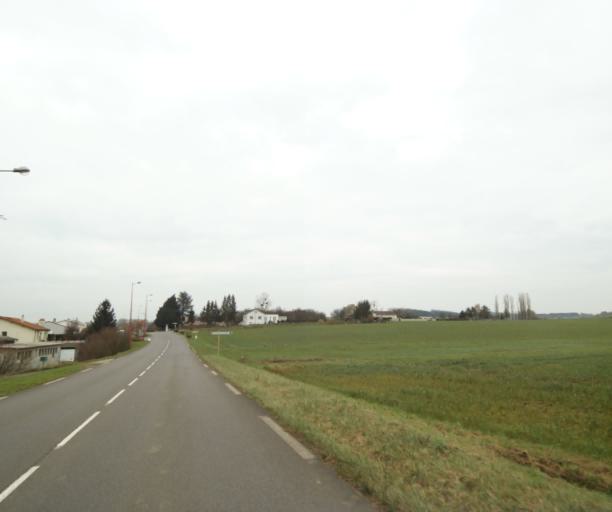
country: FR
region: Lorraine
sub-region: Departement de Meurthe-et-Moselle
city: Mancieulles
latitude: 49.2909
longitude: 5.8881
